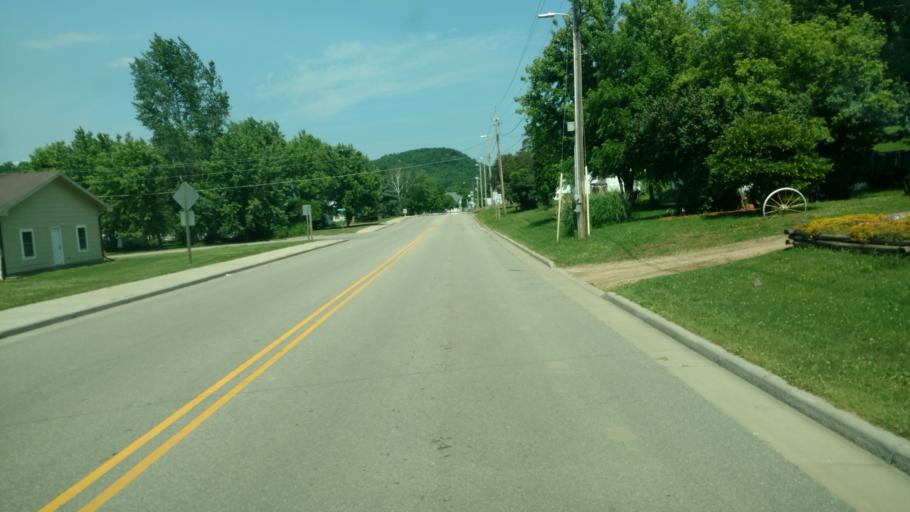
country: US
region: Wisconsin
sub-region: Vernon County
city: Viroqua
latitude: 43.5039
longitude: -90.6784
